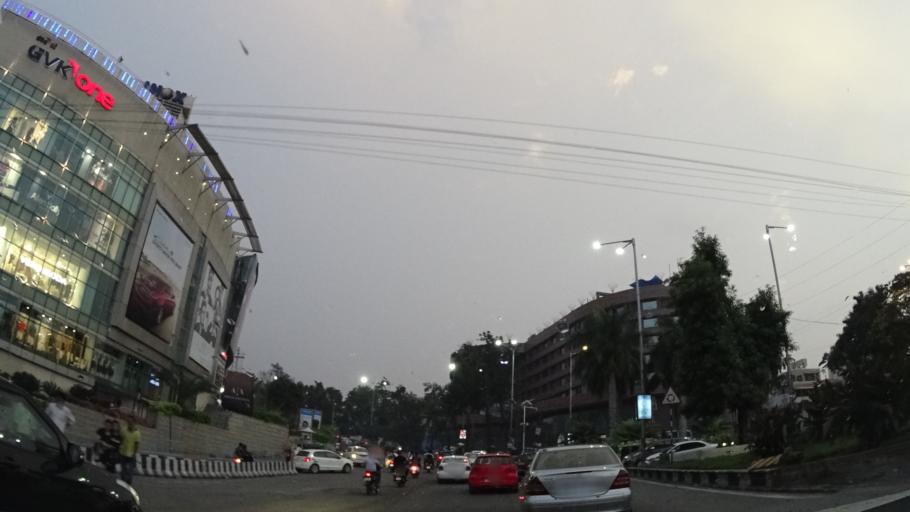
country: IN
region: Telangana
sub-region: Hyderabad
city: Hyderabad
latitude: 17.4203
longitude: 78.4483
